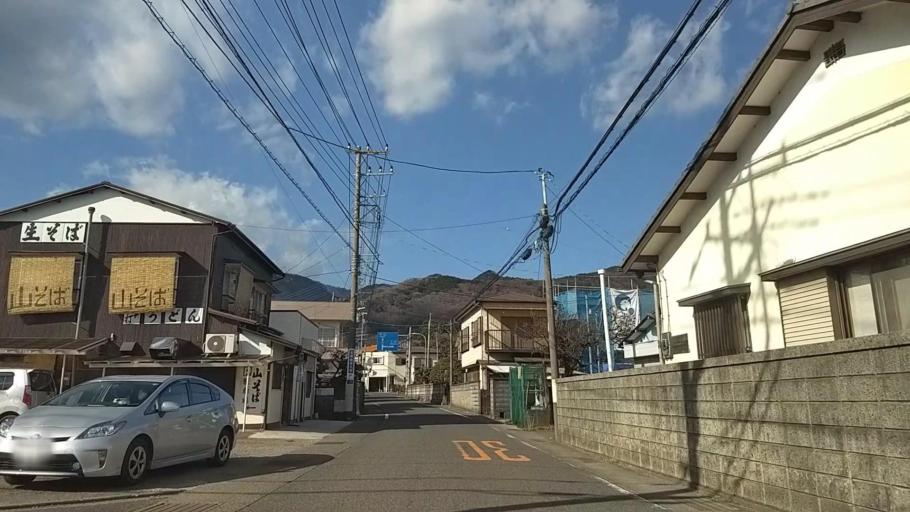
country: JP
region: Kanagawa
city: Isehara
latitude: 35.4131
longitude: 139.2851
